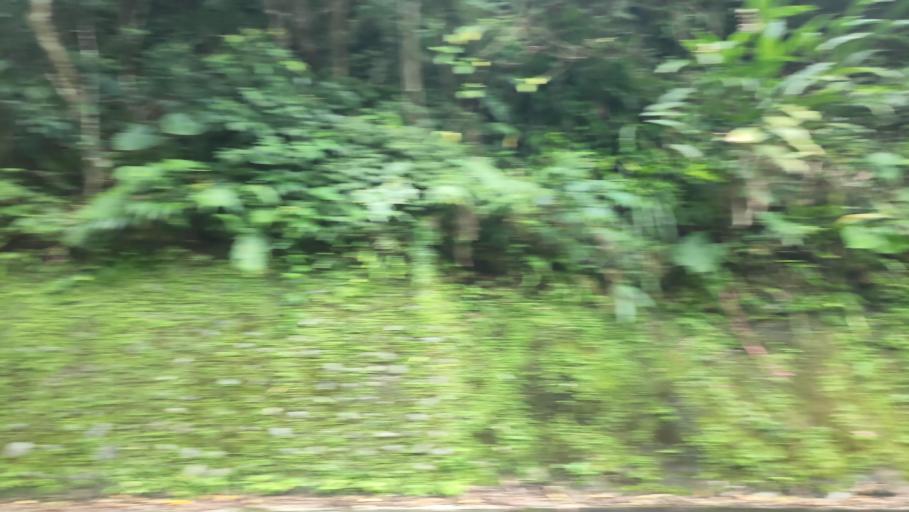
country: TW
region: Taiwan
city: Daxi
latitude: 24.8475
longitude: 121.4477
